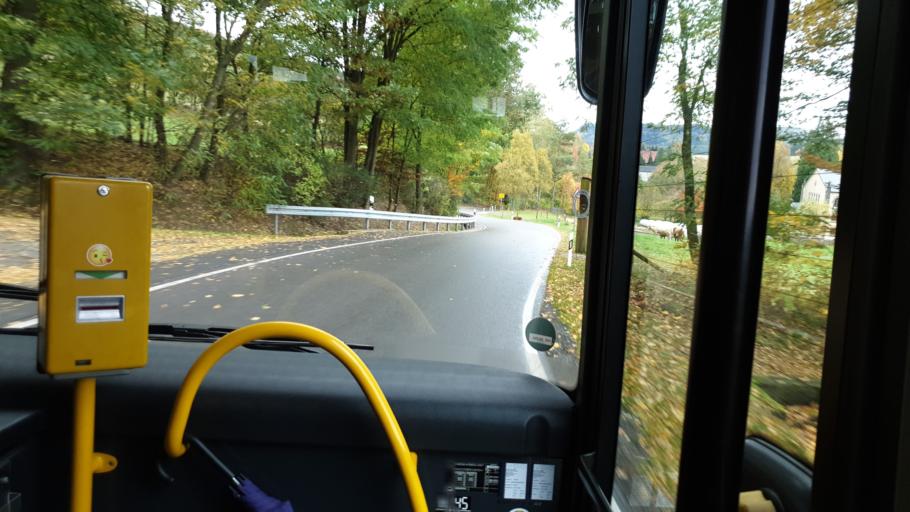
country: DE
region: Saxony
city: Kurort Gohrisch
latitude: 50.8884
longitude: 14.1113
